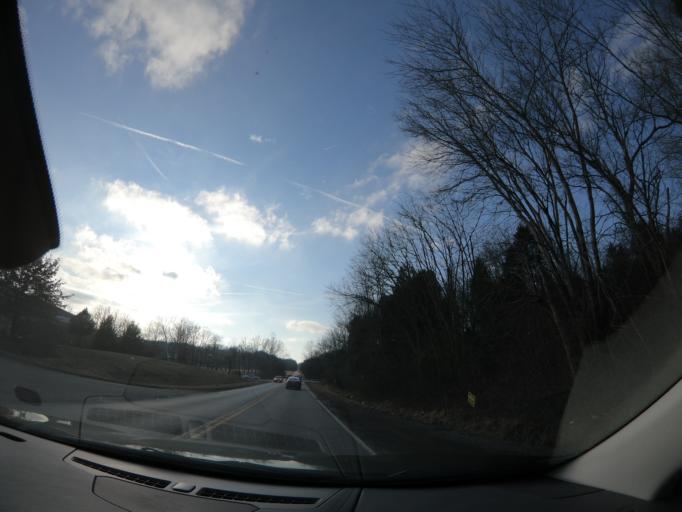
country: US
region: Kentucky
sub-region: Jefferson County
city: Middletown
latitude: 38.1909
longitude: -85.4858
